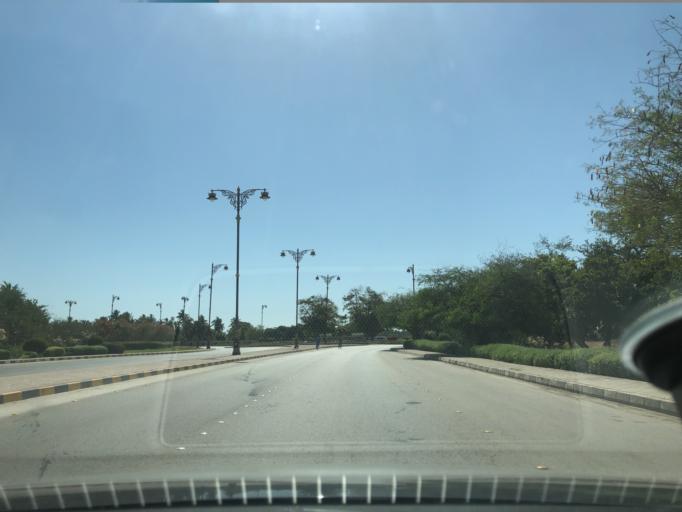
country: OM
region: Zufar
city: Salalah
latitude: 17.0278
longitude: 54.1434
